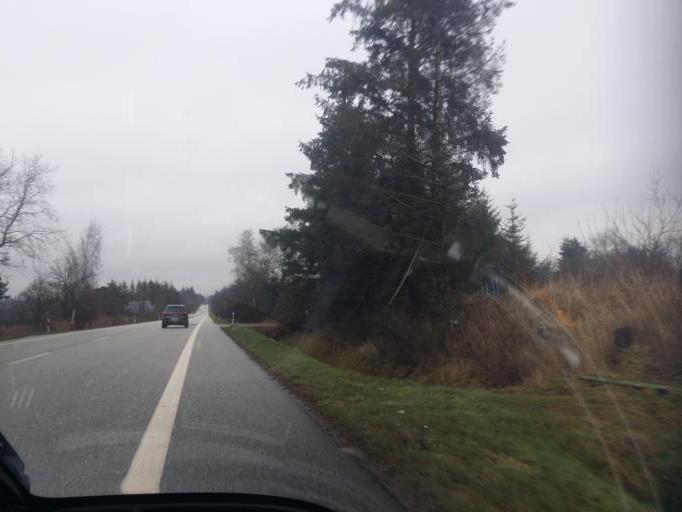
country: DE
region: Schleswig-Holstein
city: Bordelum
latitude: 54.6476
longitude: 8.9465
